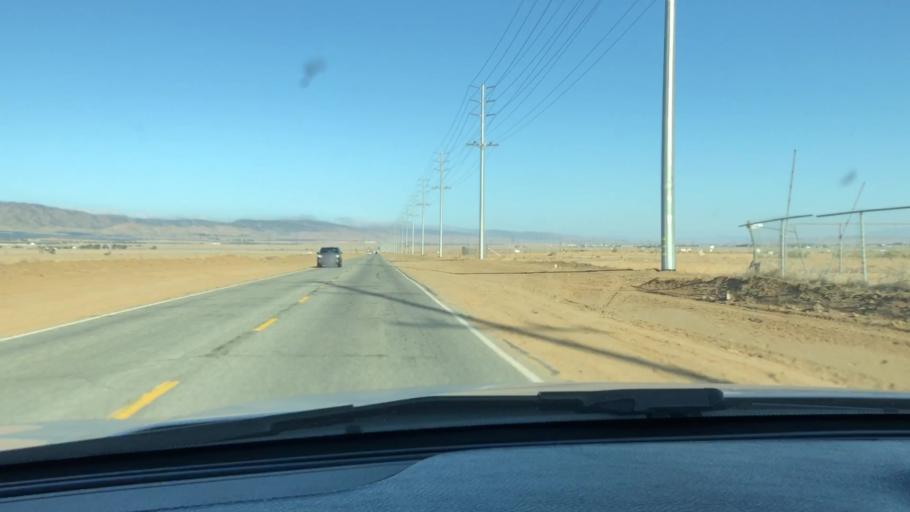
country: US
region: California
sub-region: Los Angeles County
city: Quartz Hill
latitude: 34.6747
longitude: -118.2439
